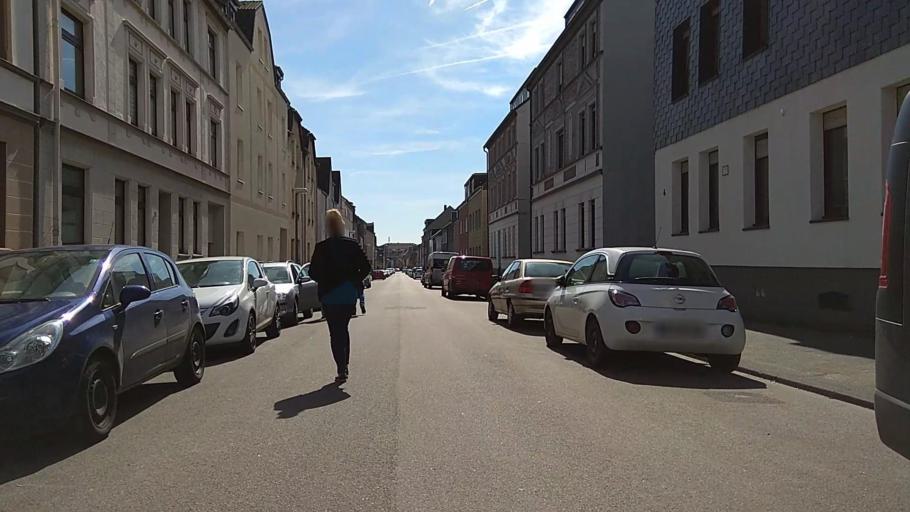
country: DE
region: North Rhine-Westphalia
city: Herten
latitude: 51.5692
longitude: 7.0818
